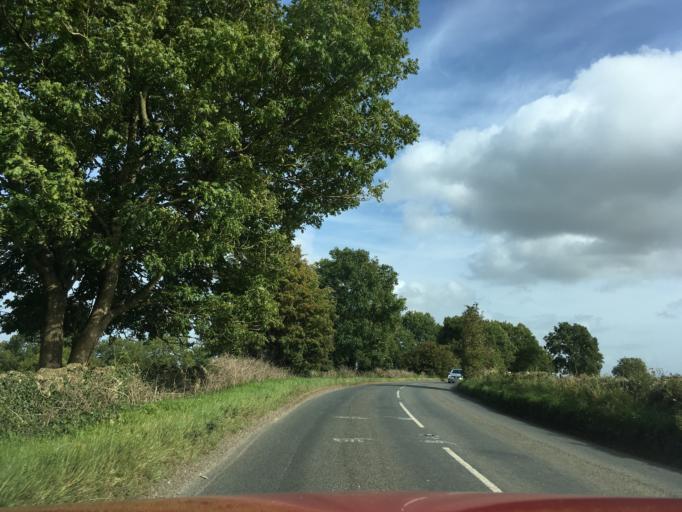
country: GB
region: England
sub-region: Gloucestershire
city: Stonehouse
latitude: 51.6988
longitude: -2.2866
